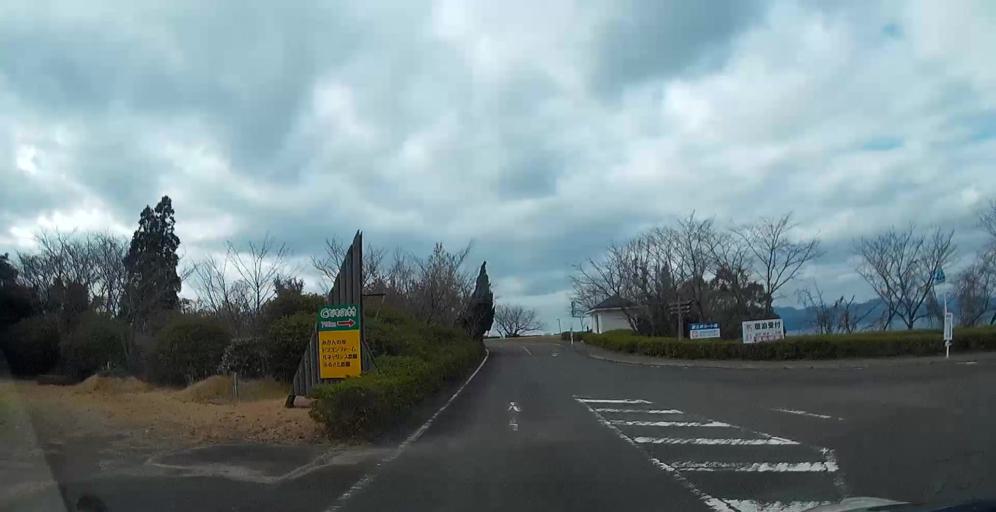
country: JP
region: Kumamoto
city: Minamata
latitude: 32.3663
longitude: 130.4919
